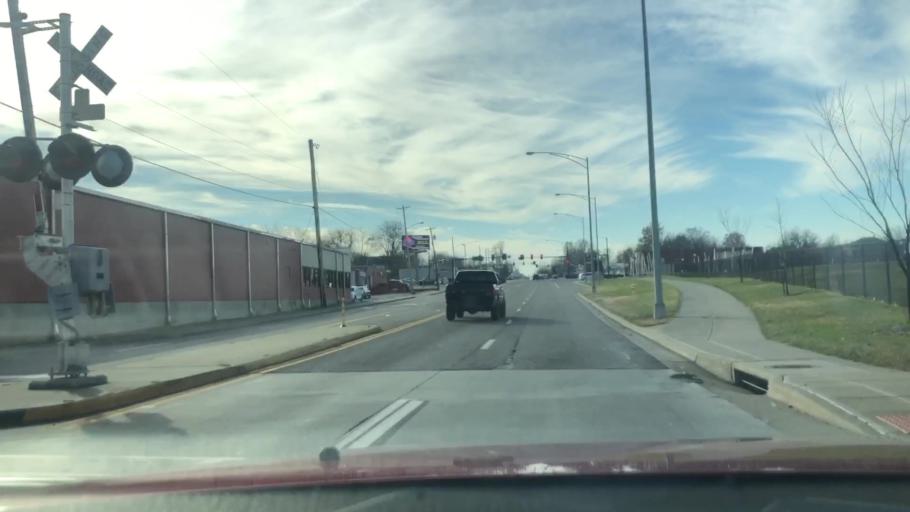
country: US
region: Missouri
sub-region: Greene County
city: Springfield
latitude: 37.2123
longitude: -93.2759
